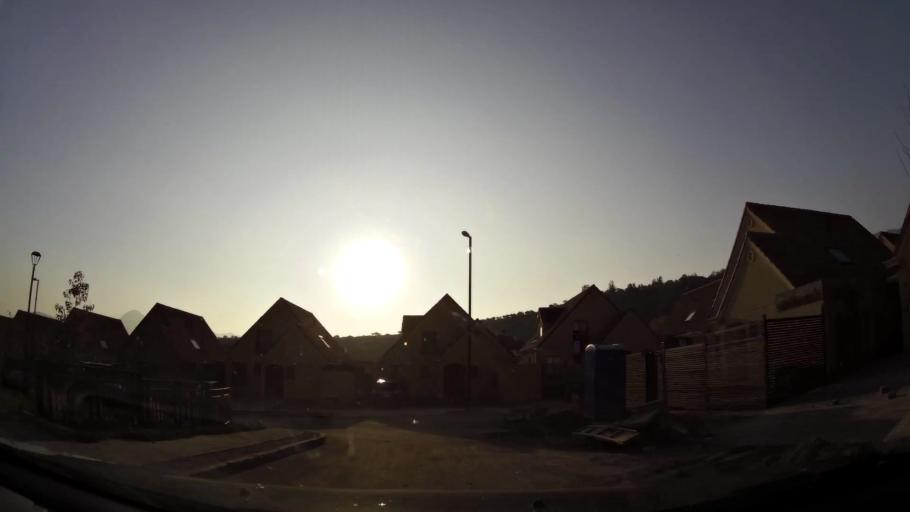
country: CL
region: Santiago Metropolitan
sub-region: Provincia de Santiago
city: Villa Presidente Frei, Nunoa, Santiago, Chile
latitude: -33.3279
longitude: -70.5039
